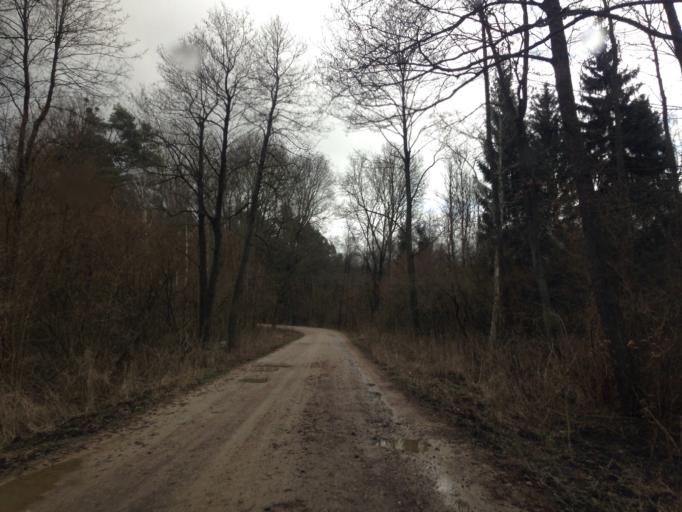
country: PL
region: Kujawsko-Pomorskie
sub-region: Powiat brodnicki
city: Gorzno
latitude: 53.2274
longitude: 19.6628
